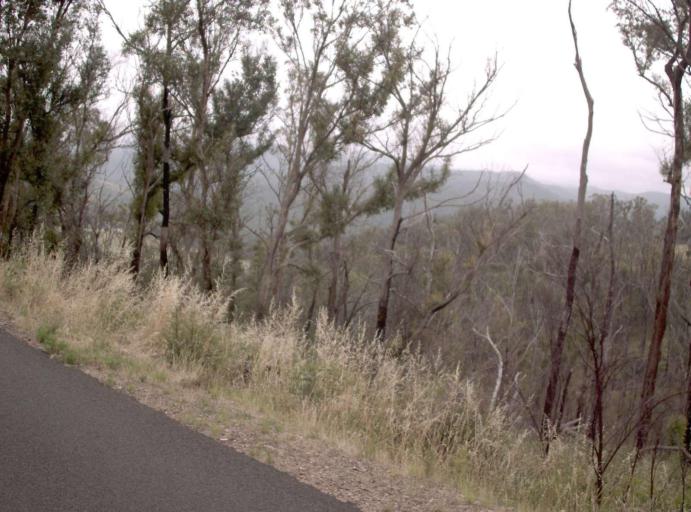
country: AU
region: Victoria
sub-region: Wellington
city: Heyfield
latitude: -37.8267
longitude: 146.6773
